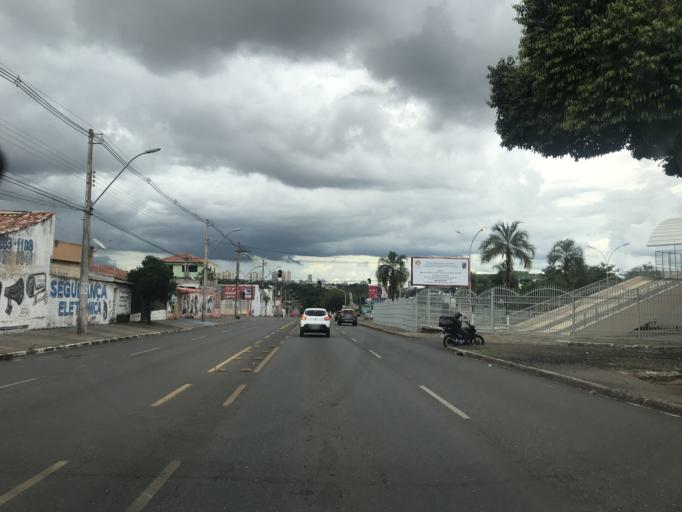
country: BR
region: Federal District
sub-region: Brasilia
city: Brasilia
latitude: -15.8437
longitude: -48.0495
